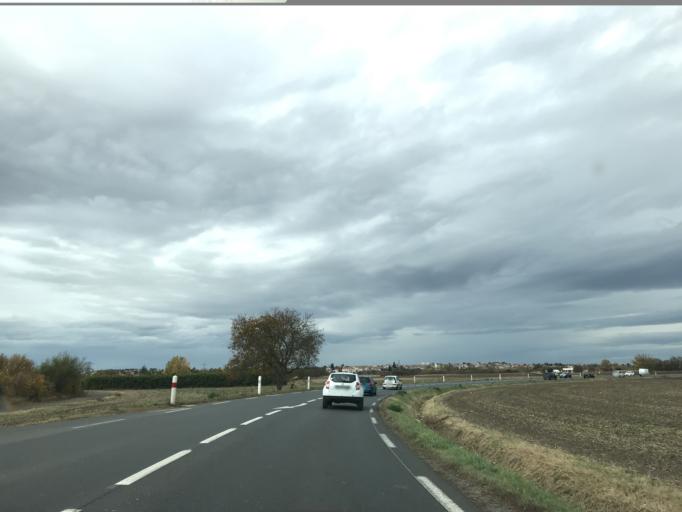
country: FR
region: Auvergne
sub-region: Departement du Puy-de-Dome
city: Dallet
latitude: 45.7812
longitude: 3.2482
